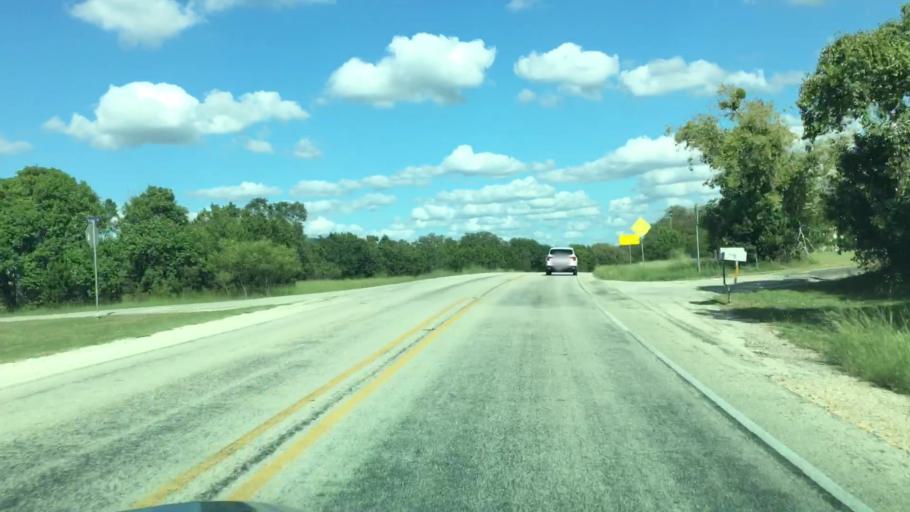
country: US
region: Texas
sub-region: Blanco County
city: Blanco
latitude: 30.0924
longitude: -98.4138
